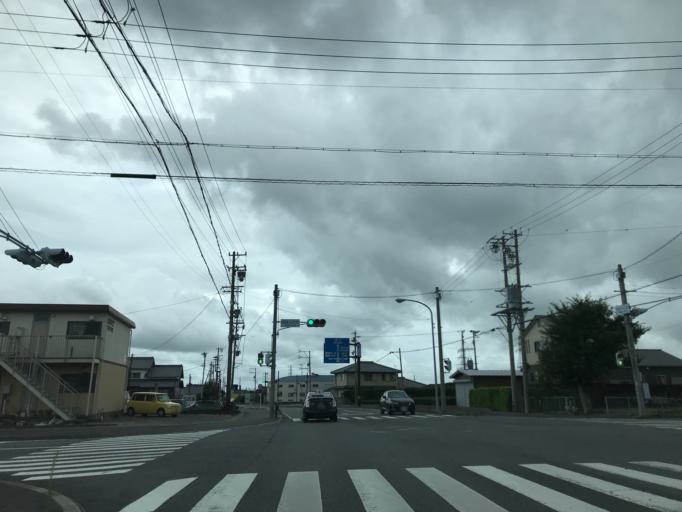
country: JP
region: Shizuoka
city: Kanaya
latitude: 34.8048
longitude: 138.1351
